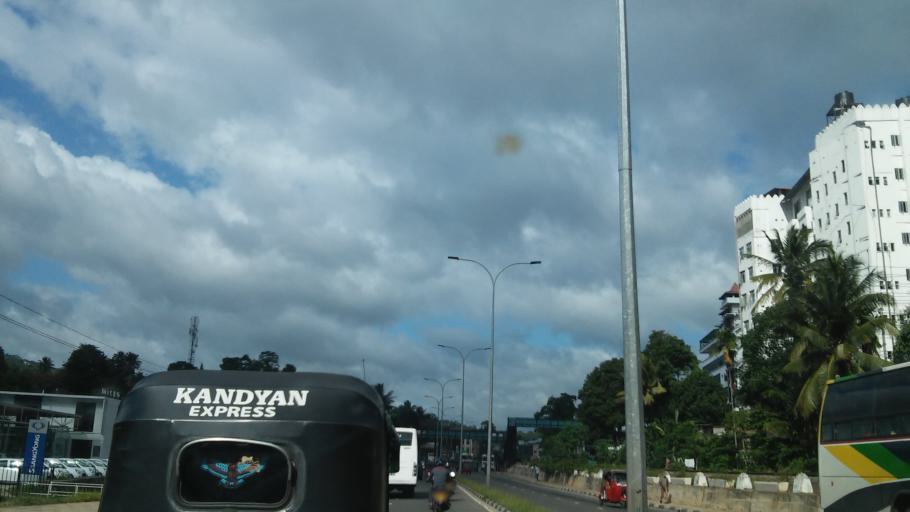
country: LK
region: Central
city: Kandy
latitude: 7.2777
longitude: 80.6171
